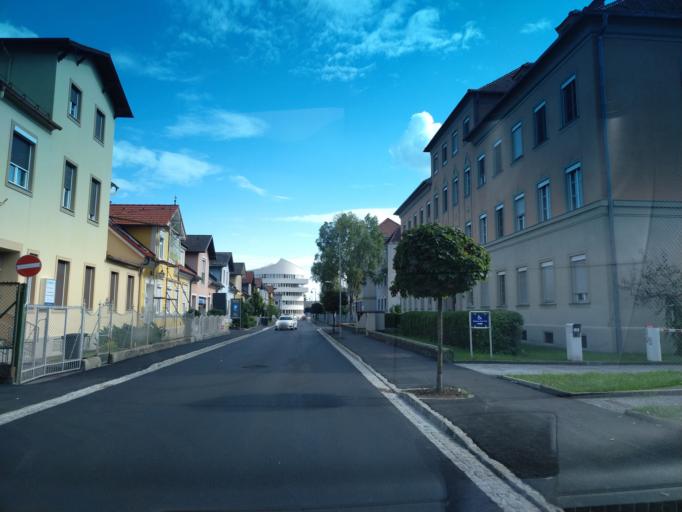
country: AT
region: Styria
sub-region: Politischer Bezirk Leibnitz
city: Leibnitz
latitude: 46.7797
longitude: 15.5381
